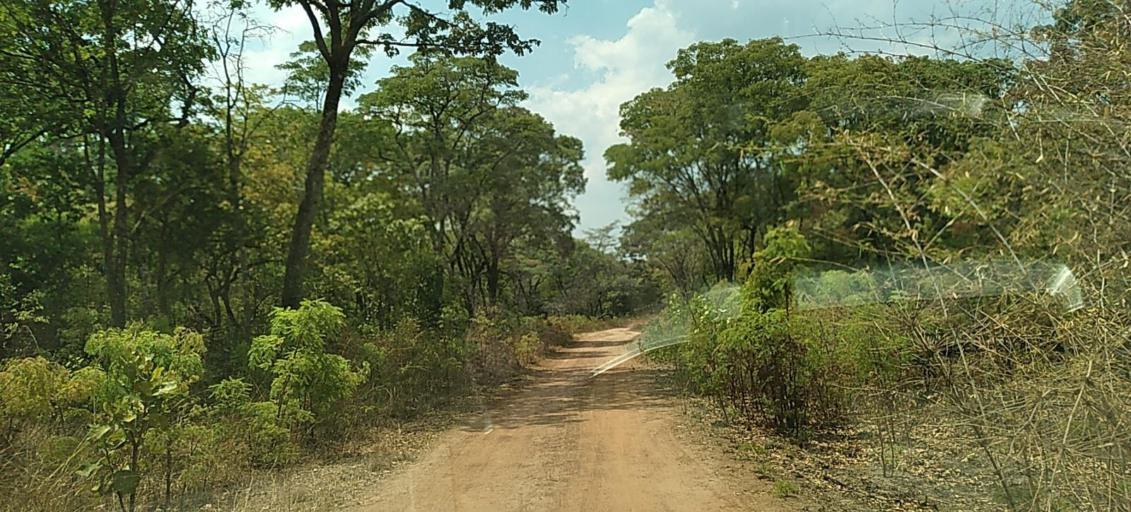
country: ZM
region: Copperbelt
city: Chingola
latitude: -12.7615
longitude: 27.7067
